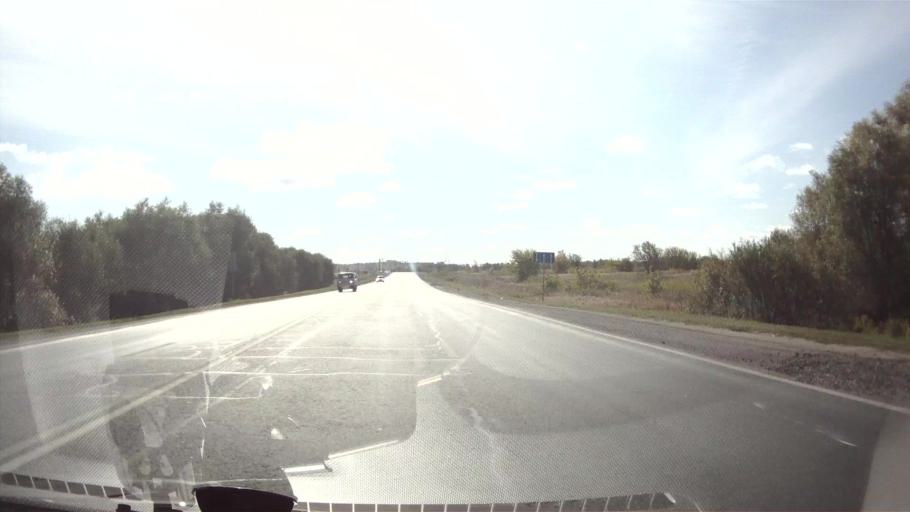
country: RU
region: Ulyanovsk
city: Isheyevka
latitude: 54.3023
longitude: 48.2436
